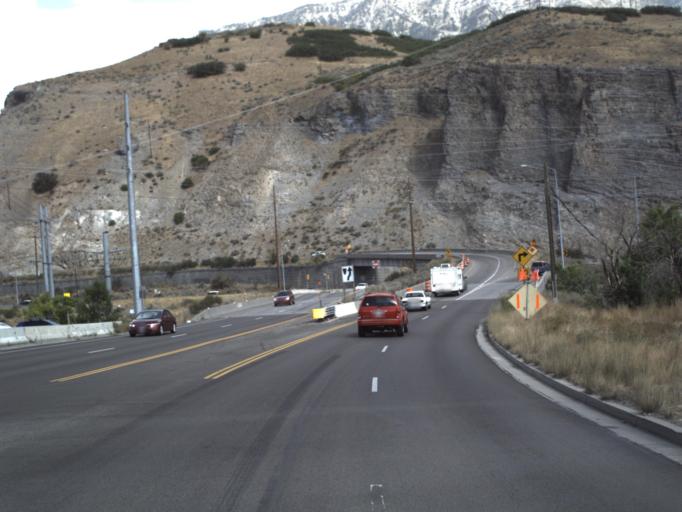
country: US
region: Utah
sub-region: Utah County
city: Orem
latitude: 40.3128
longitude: -111.6611
